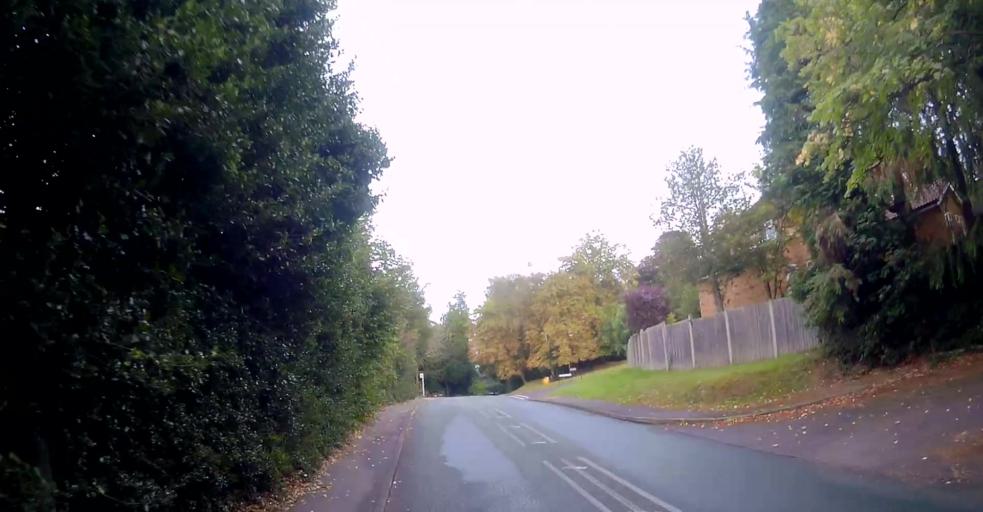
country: GB
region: England
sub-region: Surrey
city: Woking
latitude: 51.3133
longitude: -0.5814
